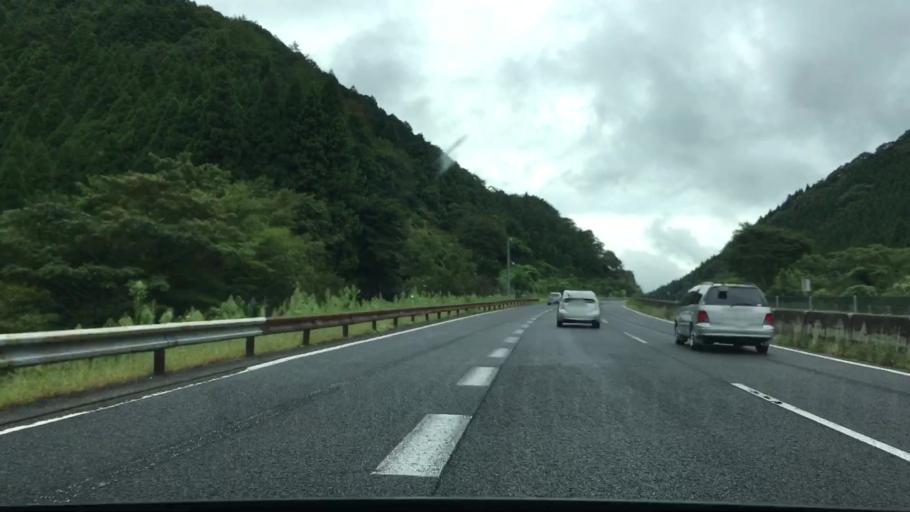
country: JP
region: Hyogo
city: Yamazakicho-nakabirose
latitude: 35.0385
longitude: 134.4720
